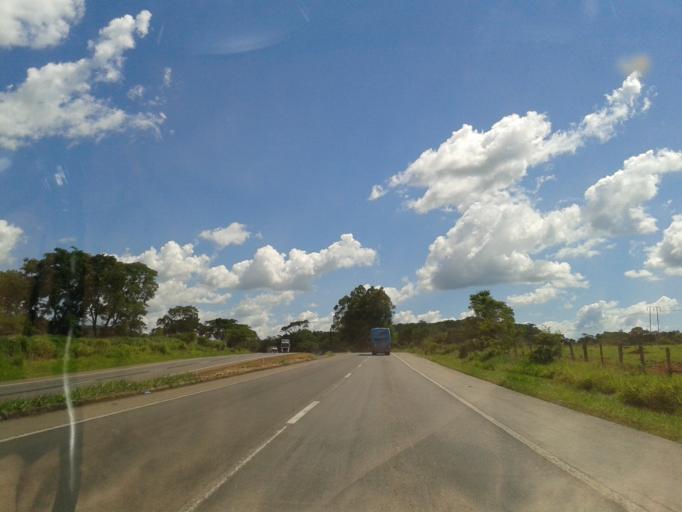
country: BR
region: Goias
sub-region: Pontalina
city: Pontalina
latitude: -17.4380
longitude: -49.2312
